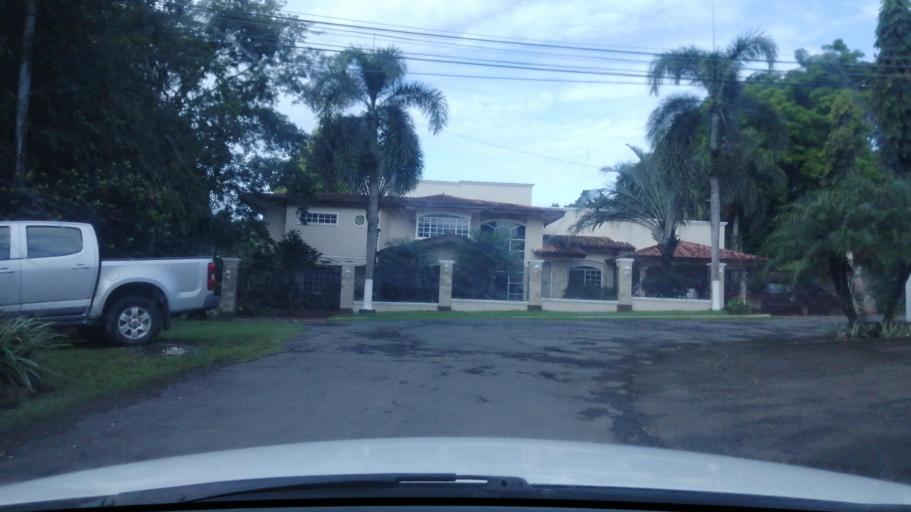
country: PA
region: Chiriqui
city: Mata del Nance
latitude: 8.4578
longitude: -82.4133
